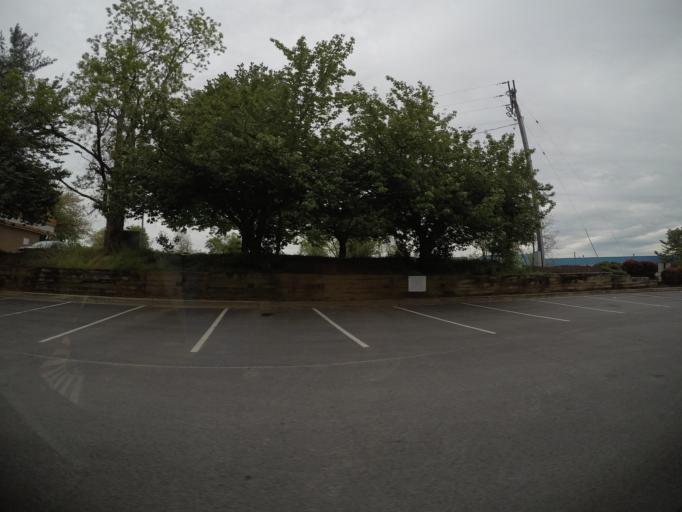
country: US
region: Maryland
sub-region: Howard County
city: Savage
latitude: 39.1763
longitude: -76.8368
